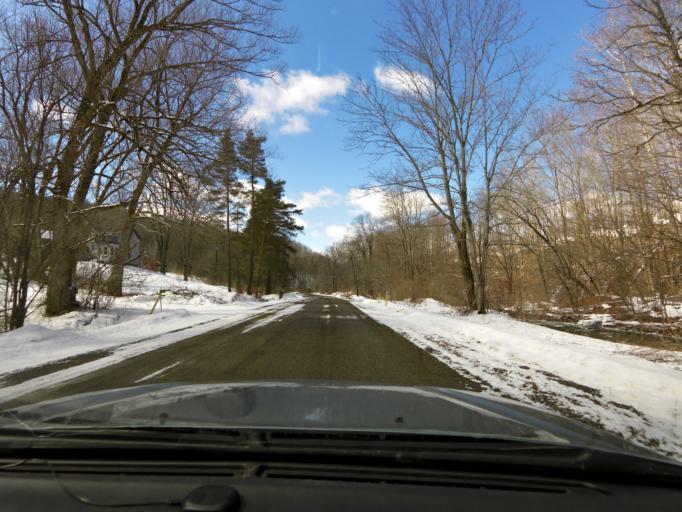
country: US
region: New York
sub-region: Cattaraugus County
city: Franklinville
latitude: 42.3432
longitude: -78.4183
